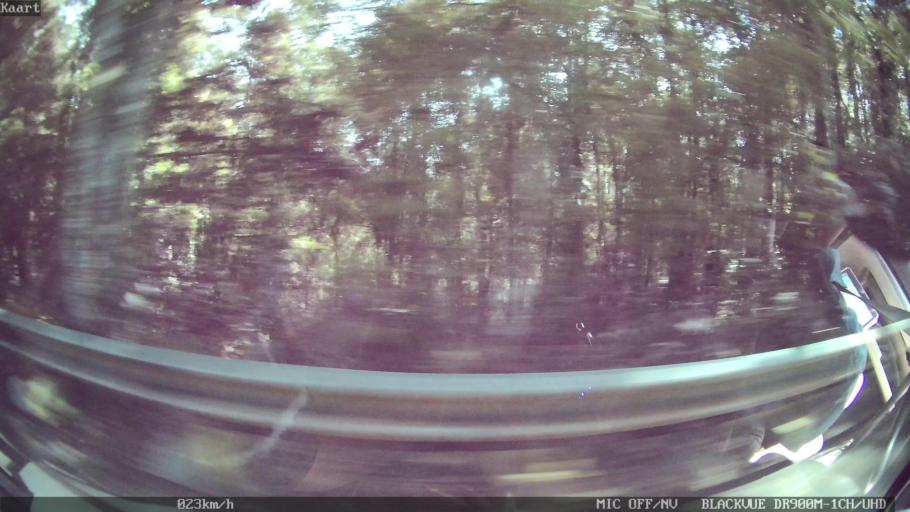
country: ID
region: Bali
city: Banjar Kedisan
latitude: -8.2891
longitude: 115.3787
